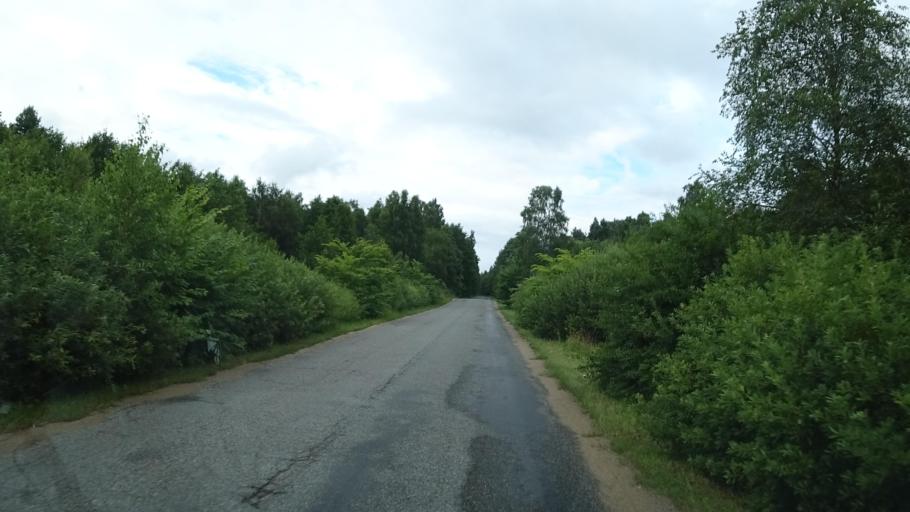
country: LV
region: Liepaja
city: Vec-Liepaja
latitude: 56.6012
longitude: 21.0322
